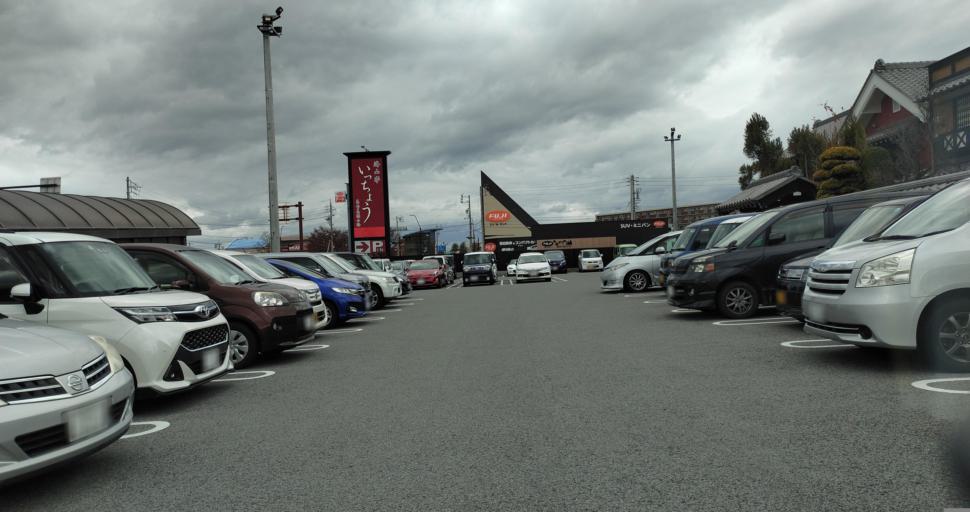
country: JP
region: Nagano
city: Komoro
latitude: 36.2853
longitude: 138.4804
